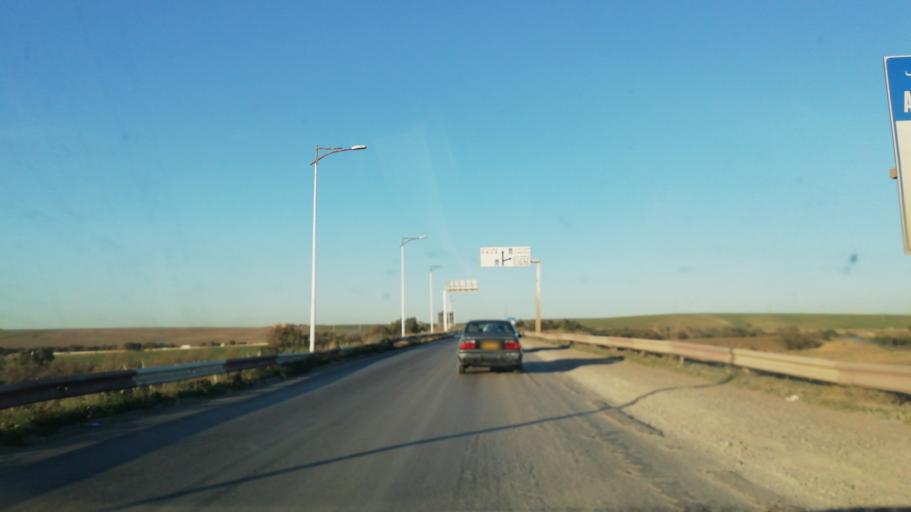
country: DZ
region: Oran
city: Sidi ech Chahmi
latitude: 35.5706
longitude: -0.5580
